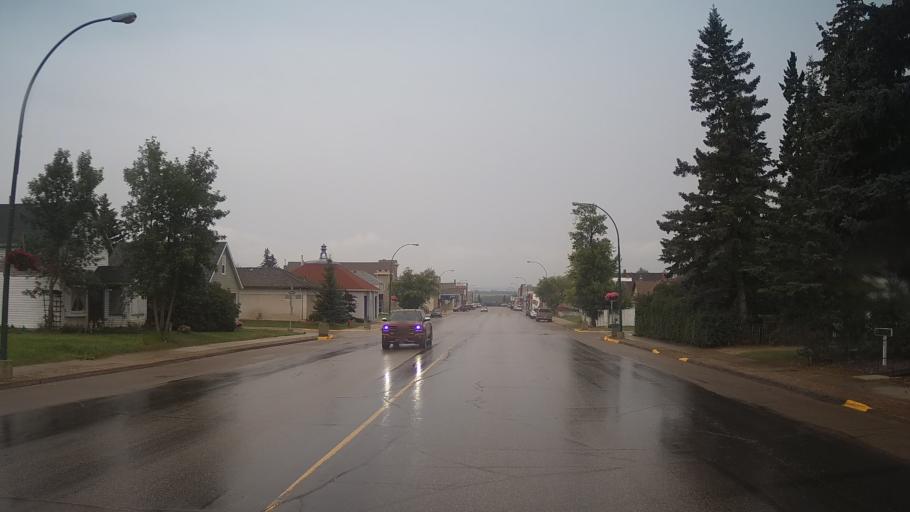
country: CA
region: Saskatchewan
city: Biggar
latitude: 52.0583
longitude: -107.9835
